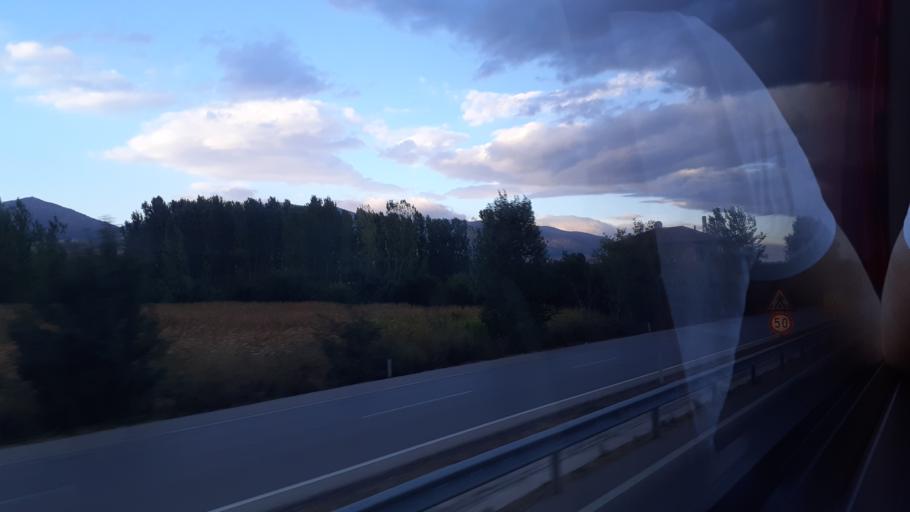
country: TR
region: Tokat
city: Dokmetepe
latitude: 40.3221
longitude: 36.2169
